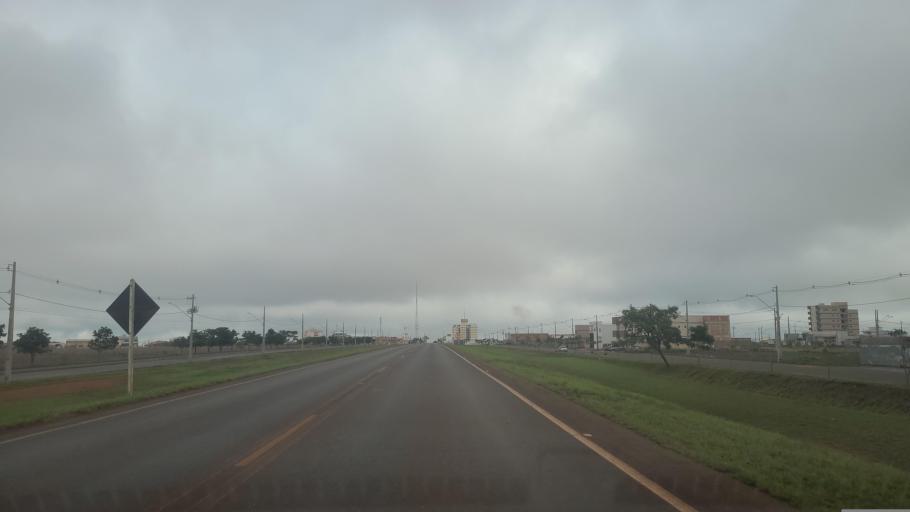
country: BR
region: Minas Gerais
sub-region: Sao Gotardo
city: Sao Gotardo
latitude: -19.2065
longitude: -46.2300
